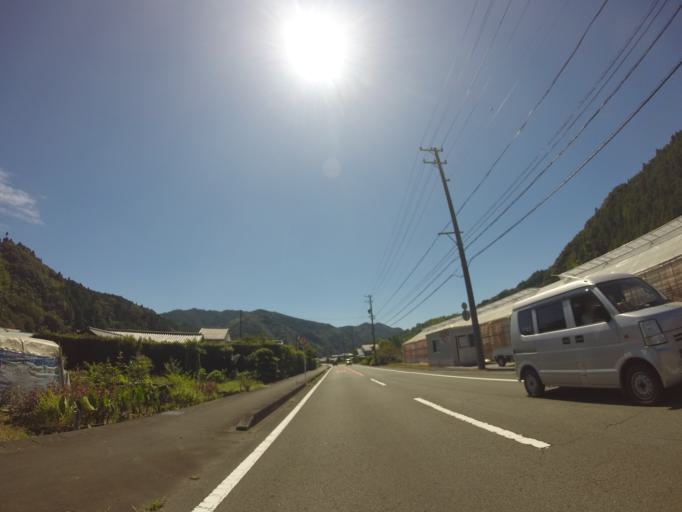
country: JP
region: Shizuoka
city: Fujieda
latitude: 34.9256
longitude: 138.2052
